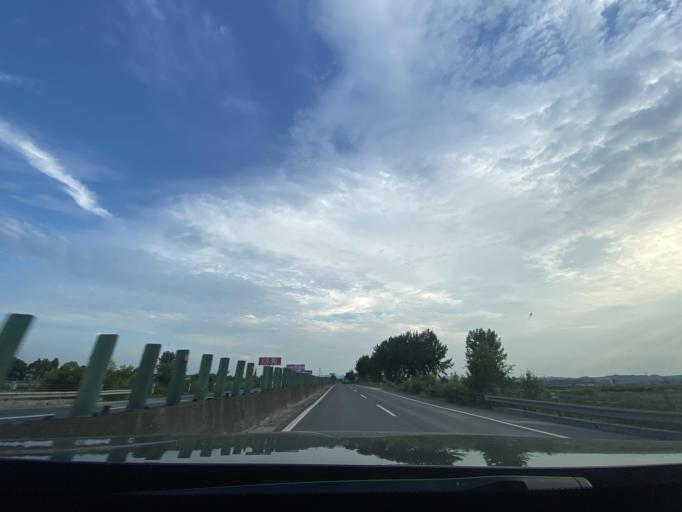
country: CN
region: Sichuan
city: Luojiang
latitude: 31.3781
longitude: 104.5489
